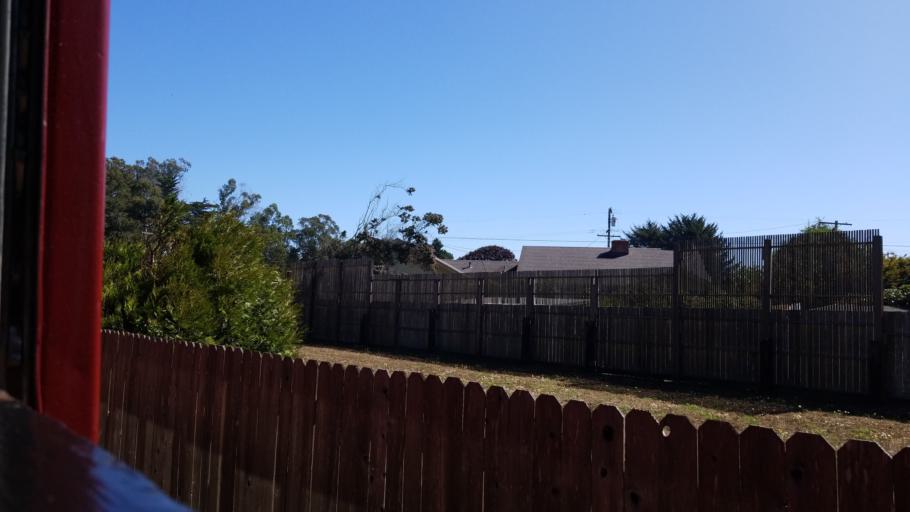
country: US
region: California
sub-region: Mendocino County
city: Fort Bragg
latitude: 39.4504
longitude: -123.8029
